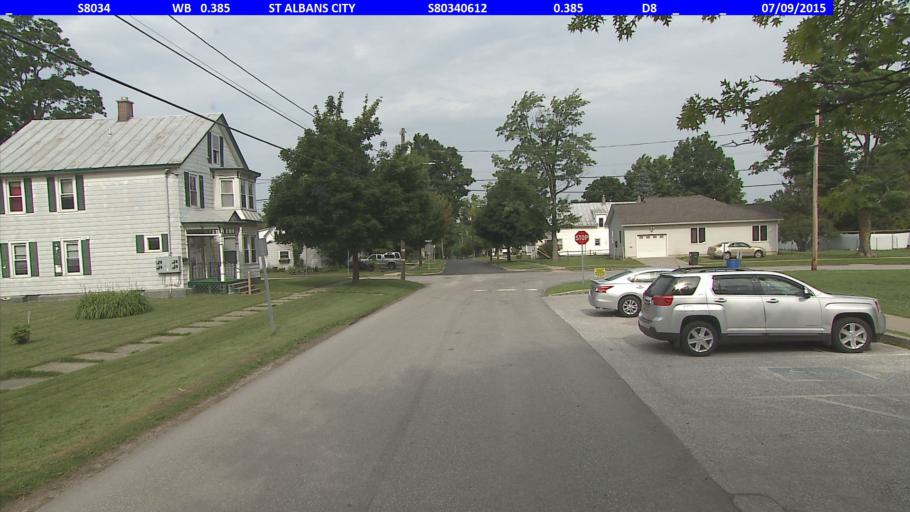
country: US
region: Vermont
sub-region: Franklin County
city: Saint Albans
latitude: 44.8047
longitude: -73.0779
